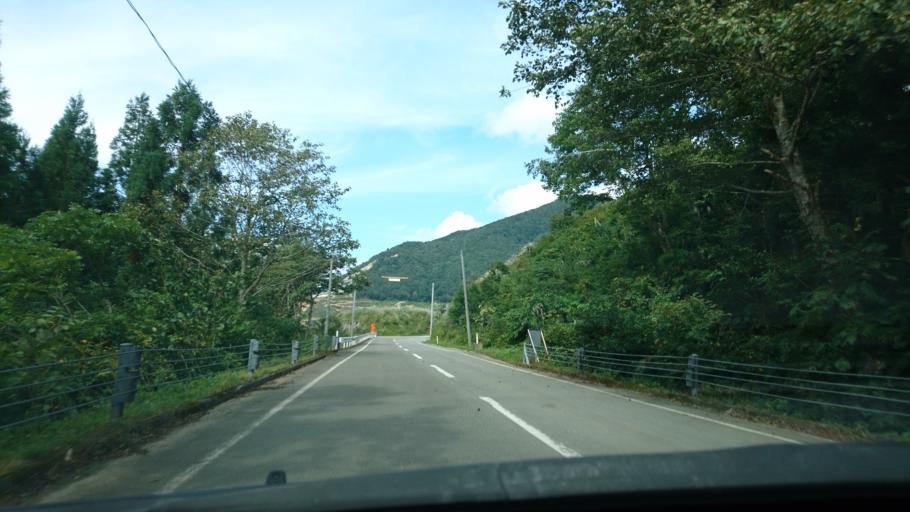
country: JP
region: Akita
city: Yuzawa
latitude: 39.0294
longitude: 140.7277
